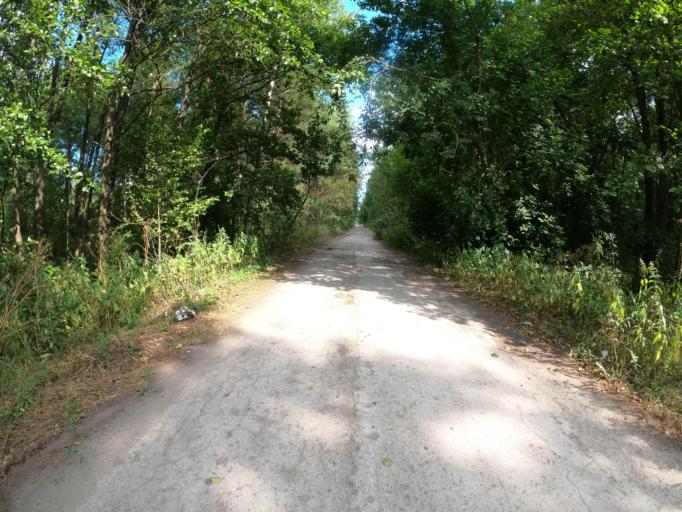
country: RU
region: Moskovskaya
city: Konobeyevo
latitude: 55.3840
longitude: 38.7033
